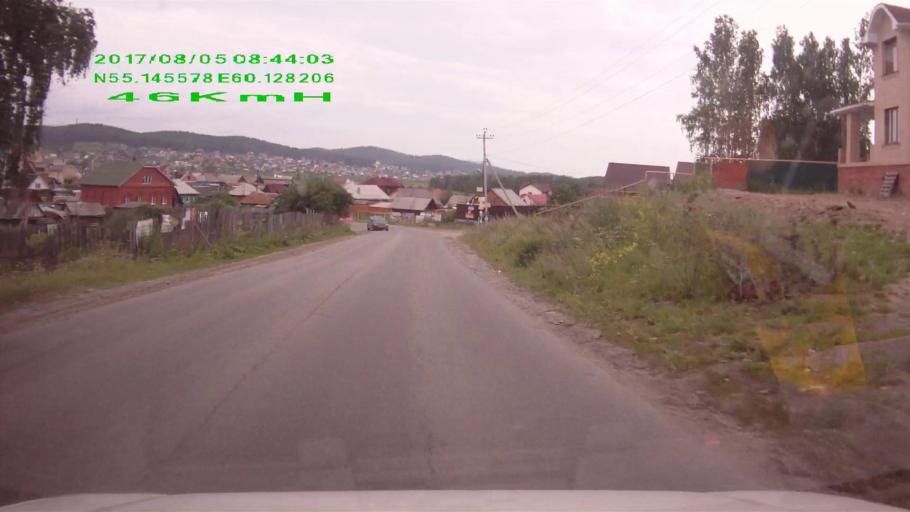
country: RU
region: Chelyabinsk
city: Turgoyak
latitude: 55.1456
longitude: 60.1280
